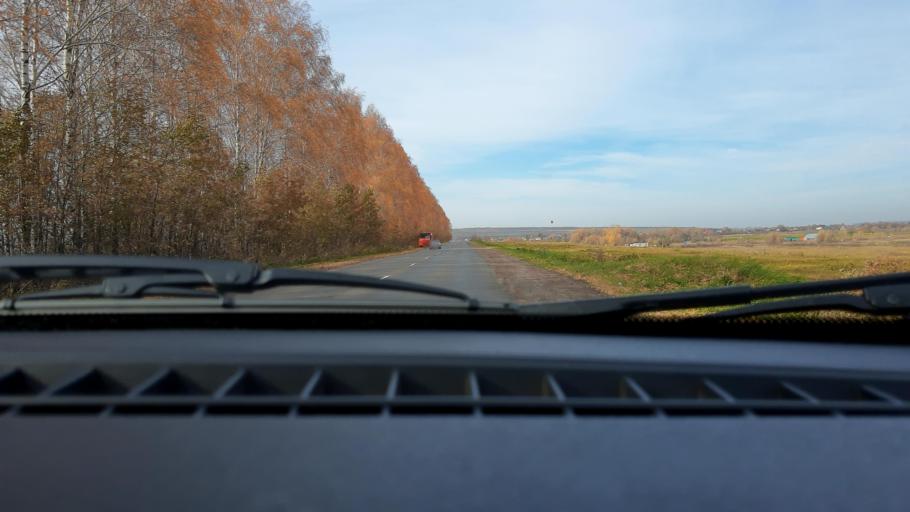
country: RU
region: Bashkortostan
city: Ufa
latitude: 54.8262
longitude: 55.9786
